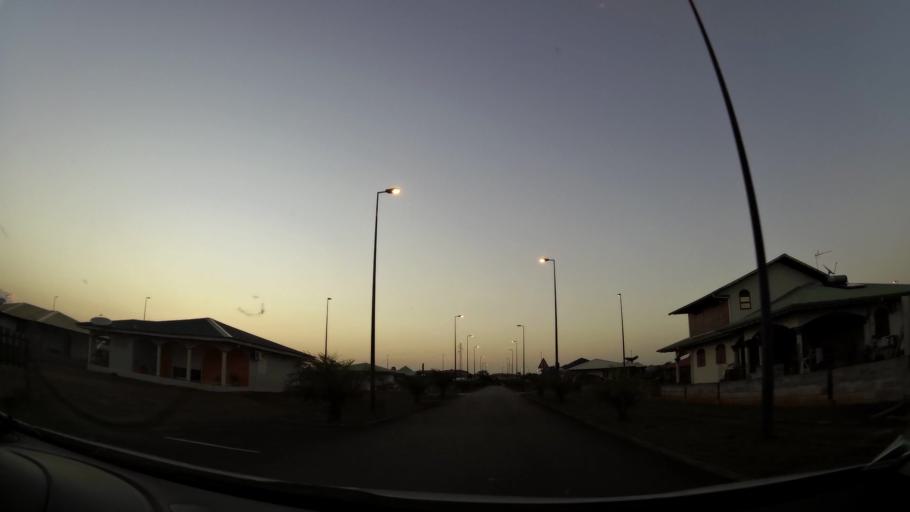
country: GF
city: Macouria
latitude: 4.9244
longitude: -52.4084
